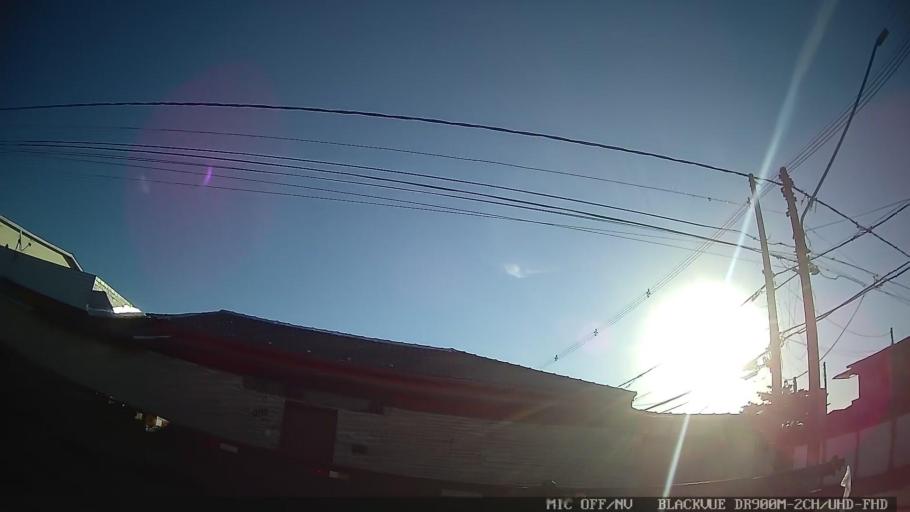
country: BR
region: Sao Paulo
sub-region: Santos
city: Santos
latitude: -23.9402
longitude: -46.2930
